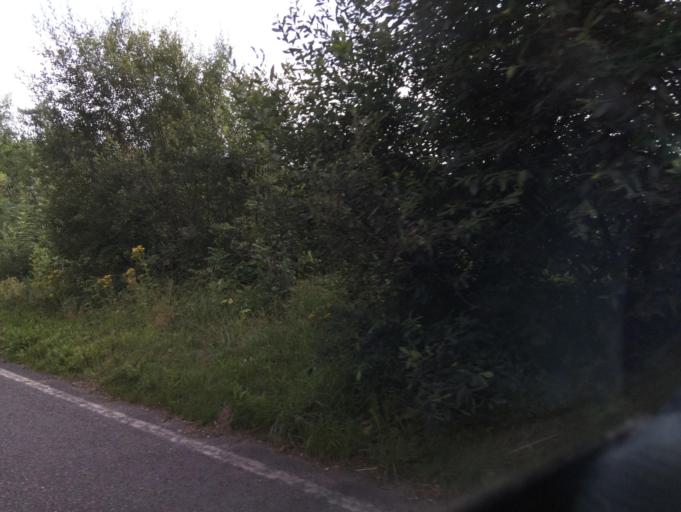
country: GB
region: England
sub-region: Hampshire
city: Marchwood
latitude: 50.8642
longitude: -1.4356
